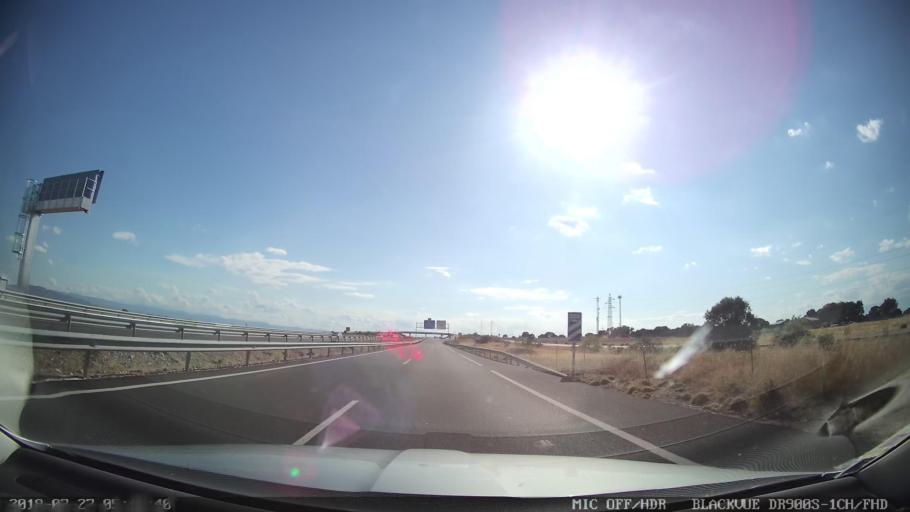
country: ES
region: Castille-La Mancha
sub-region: Province of Toledo
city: Calera y Chozas
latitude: 39.9240
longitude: -5.0335
